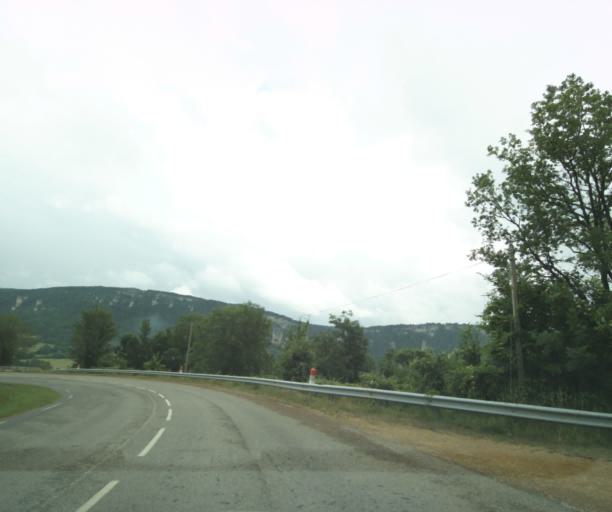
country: FR
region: Languedoc-Roussillon
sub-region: Departement de la Lozere
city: La Canourgue
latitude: 44.4175
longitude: 3.1800
